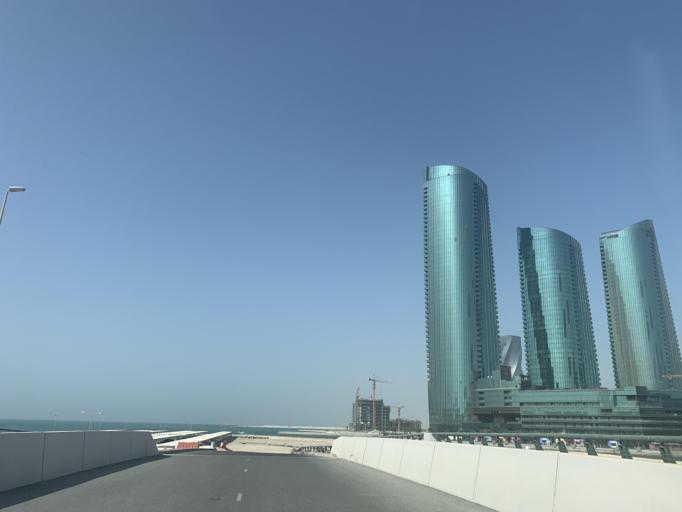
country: BH
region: Manama
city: Manama
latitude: 26.2383
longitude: 50.5703
